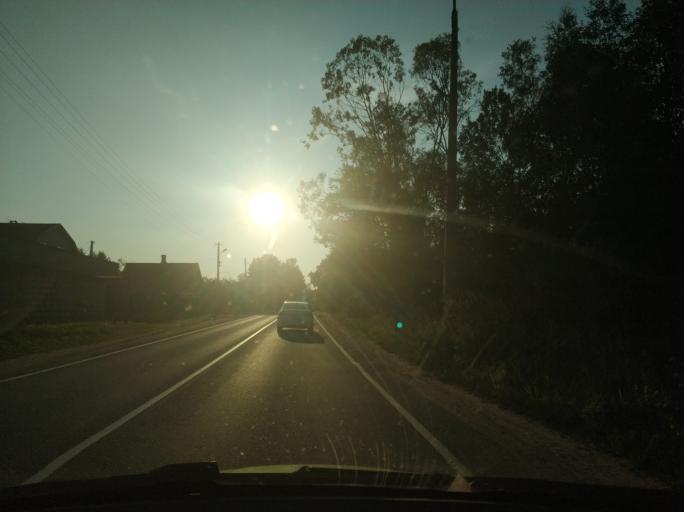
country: RU
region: Leningrad
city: Borisova Griva
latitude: 60.0823
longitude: 31.0353
